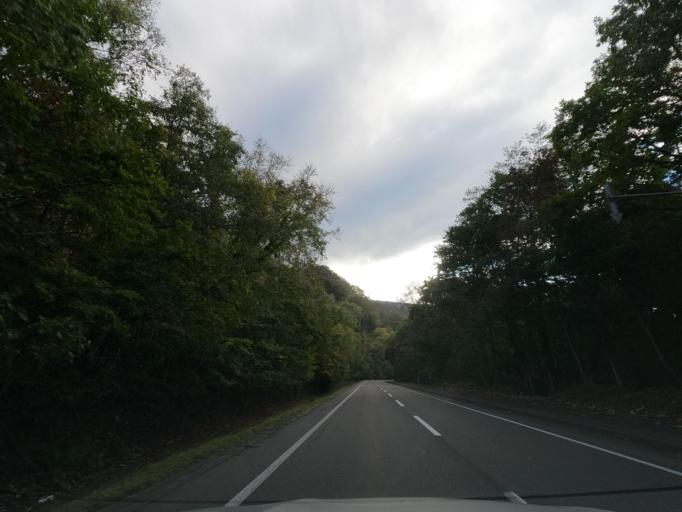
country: JP
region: Hokkaido
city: Shiraoi
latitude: 42.7049
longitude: 141.3073
